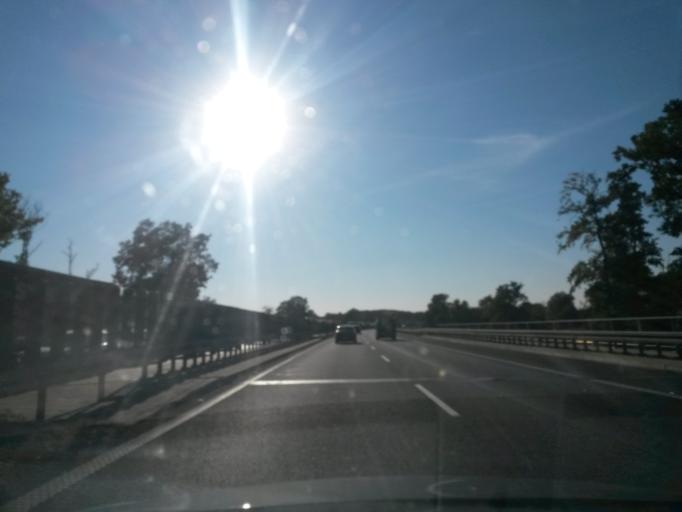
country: PL
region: Lower Silesian Voivodeship
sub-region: Powiat wroclawski
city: Katy Wroclawskie
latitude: 51.0242
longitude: 16.7814
